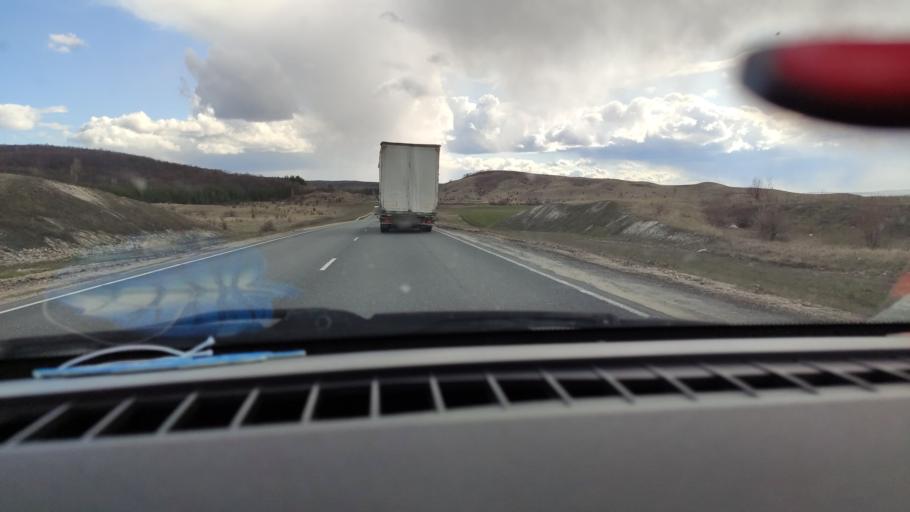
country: RU
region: Saratov
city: Alekseyevka
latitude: 52.3789
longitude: 47.9721
